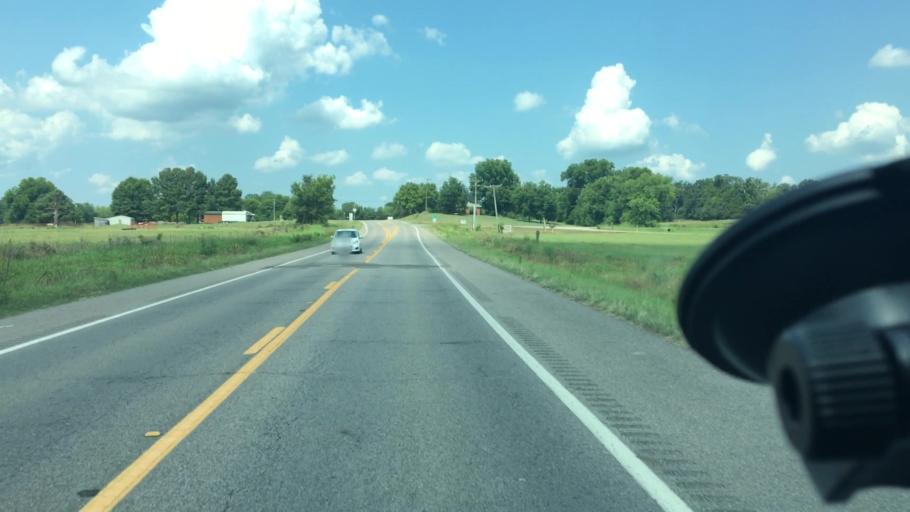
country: US
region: Arkansas
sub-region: Logan County
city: Paris
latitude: 35.2952
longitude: -93.6847
